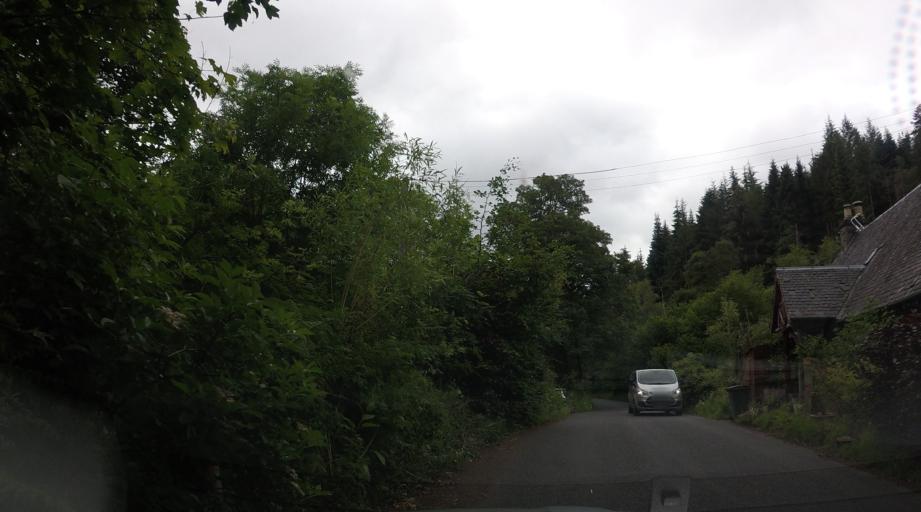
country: GB
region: Scotland
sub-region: Perth and Kinross
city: Pitlochry
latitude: 56.7275
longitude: -3.8273
